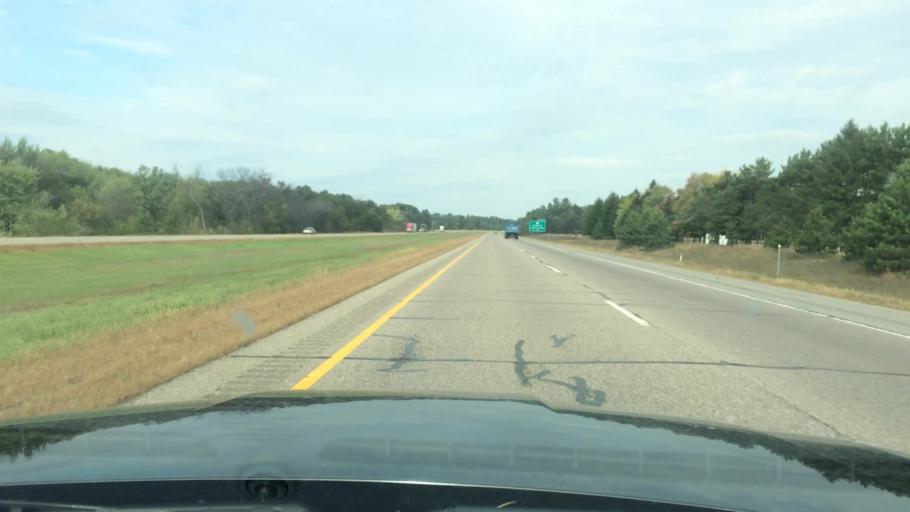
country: US
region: Wisconsin
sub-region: Portage County
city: Stevens Point
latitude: 44.6535
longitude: -89.6397
